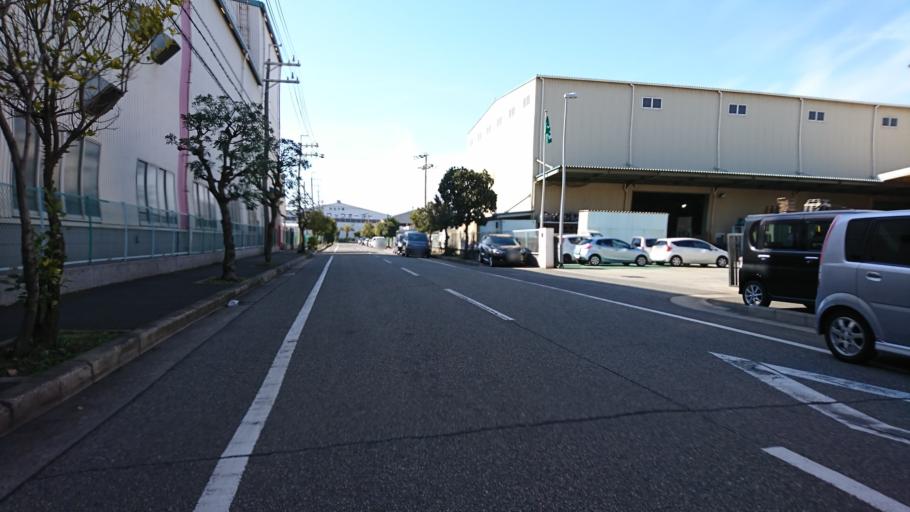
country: JP
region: Hyogo
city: Kakogawacho-honmachi
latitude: 34.6984
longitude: 134.8504
